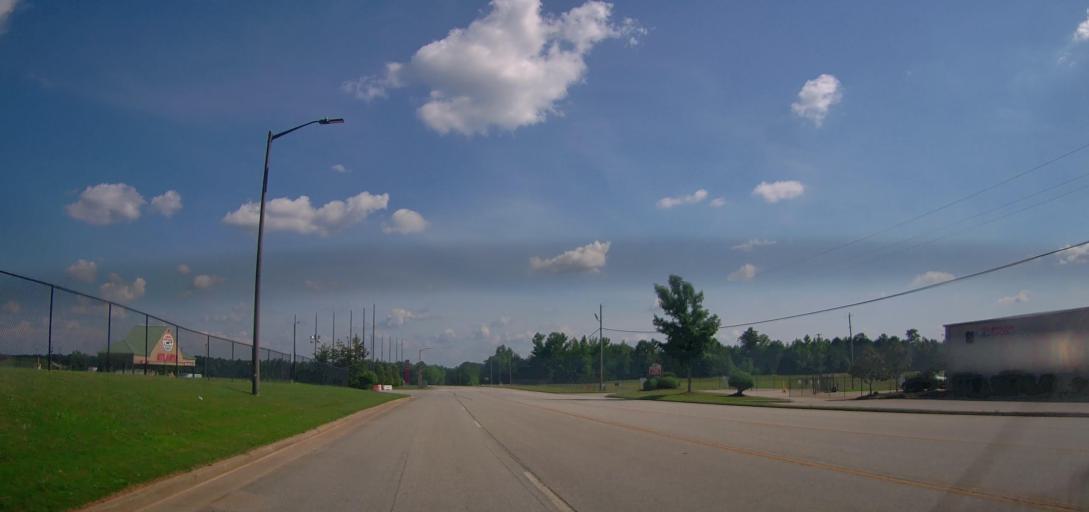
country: US
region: Georgia
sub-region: Henry County
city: Hampton
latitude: 33.3851
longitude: -84.3249
